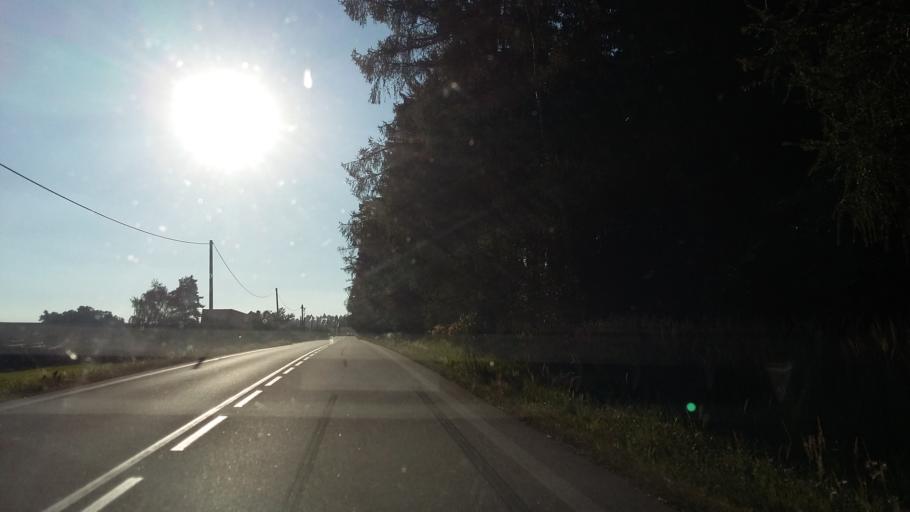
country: CZ
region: Vysocina
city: Velky Beranov
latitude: 49.3993
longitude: 15.6901
